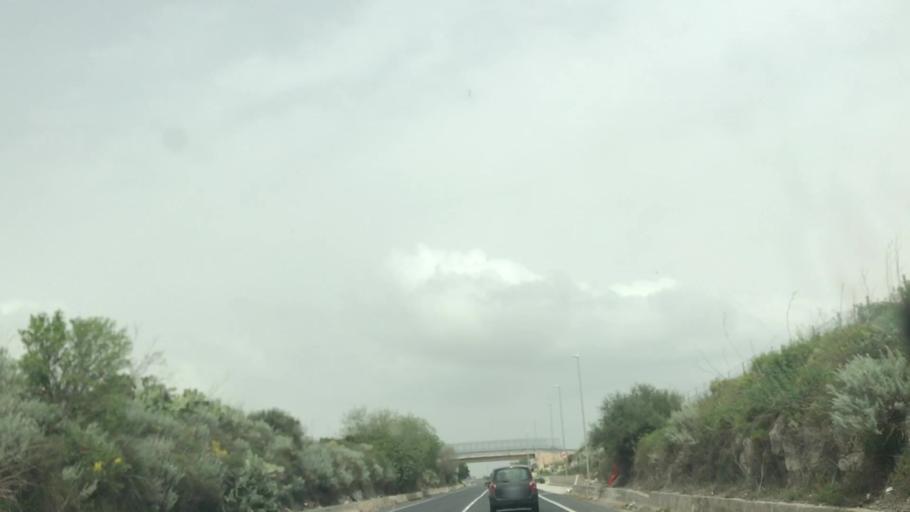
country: IT
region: Sicily
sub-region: Ragusa
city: Ragusa
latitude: 36.8767
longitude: 14.6937
